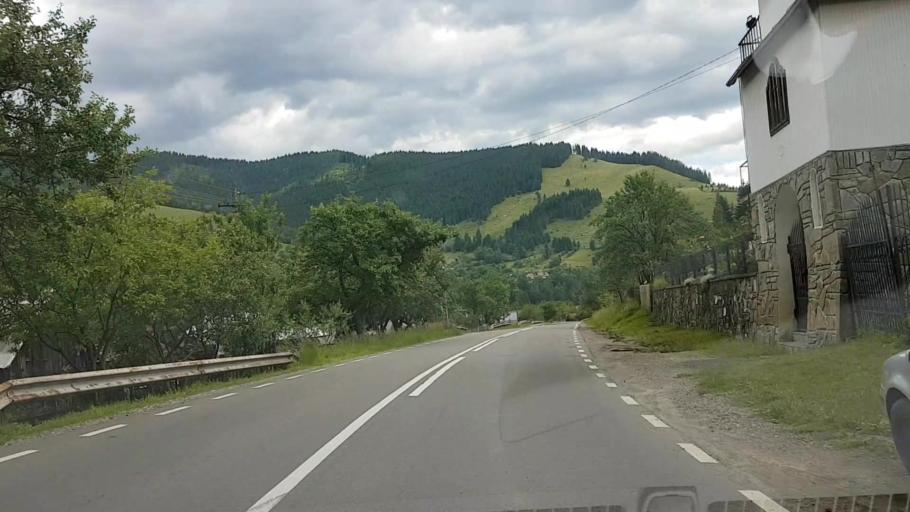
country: RO
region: Neamt
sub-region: Comuna Farcasa
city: Farcasa
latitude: 47.1532
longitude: 25.8578
